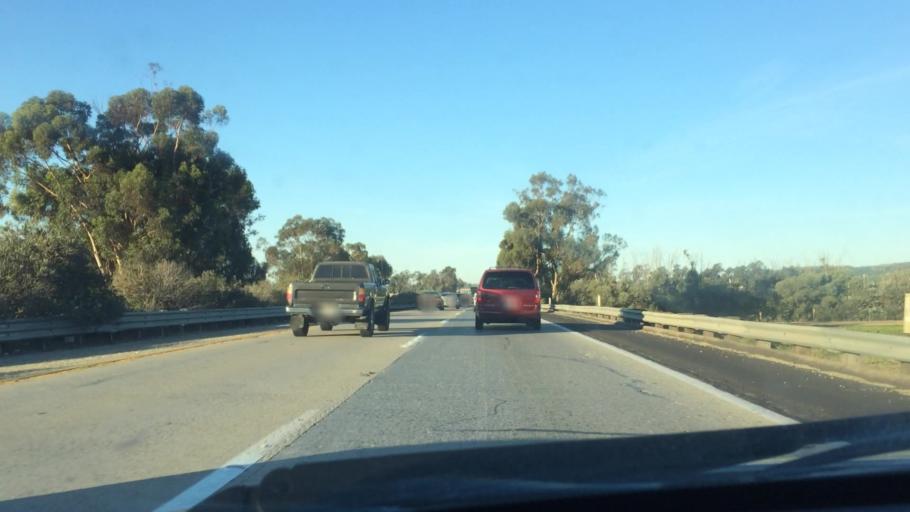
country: US
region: California
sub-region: Ventura County
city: Saticoy
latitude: 34.3145
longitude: -119.1148
